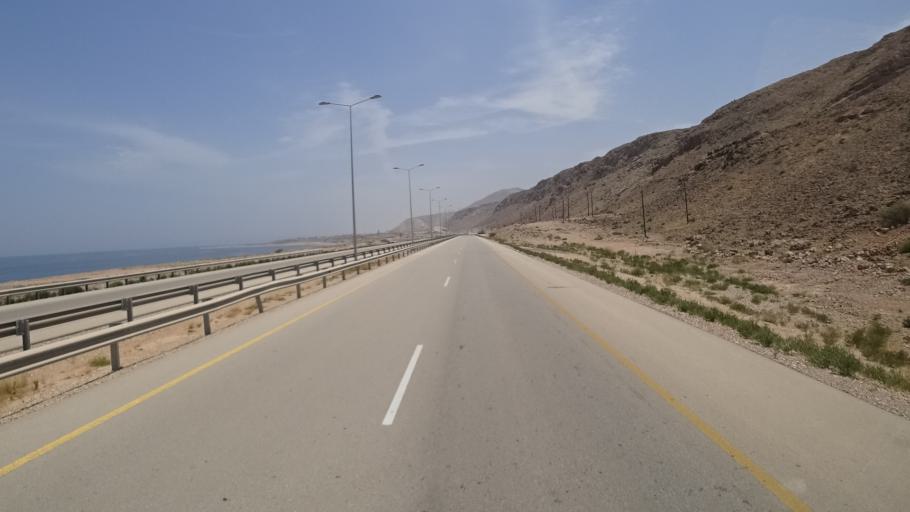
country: OM
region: Ash Sharqiyah
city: Sur
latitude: 22.7200
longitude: 59.3486
